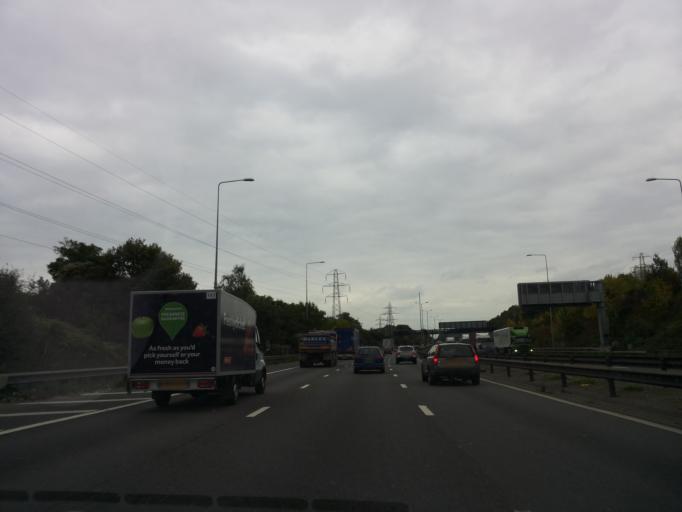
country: GB
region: England
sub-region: Kent
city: Greenhithe
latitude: 51.4313
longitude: 0.2810
